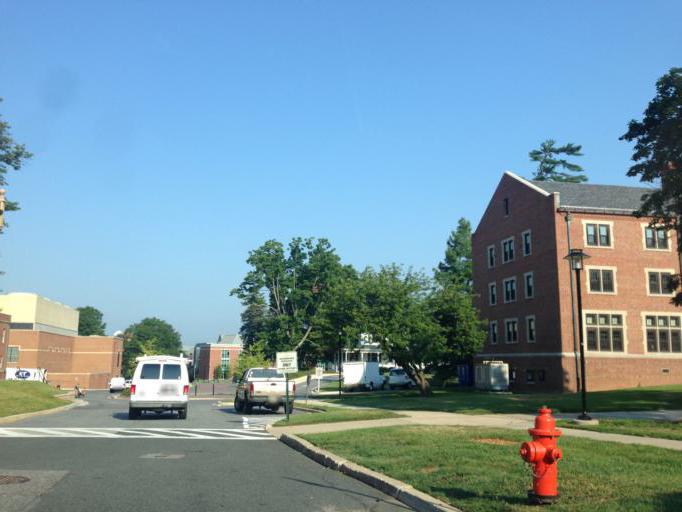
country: US
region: Maryland
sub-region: Baltimore County
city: Towson
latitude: 39.3943
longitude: -76.6049
